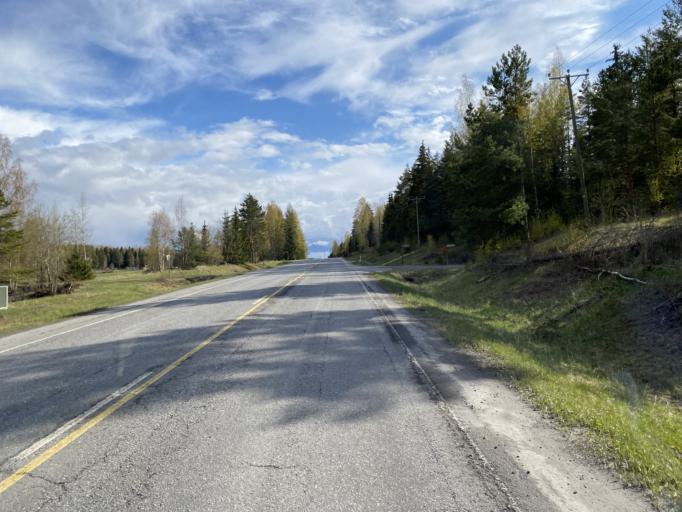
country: FI
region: Pirkanmaa
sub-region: Etelae-Pirkanmaa
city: Viiala
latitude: 61.2495
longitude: 23.7412
